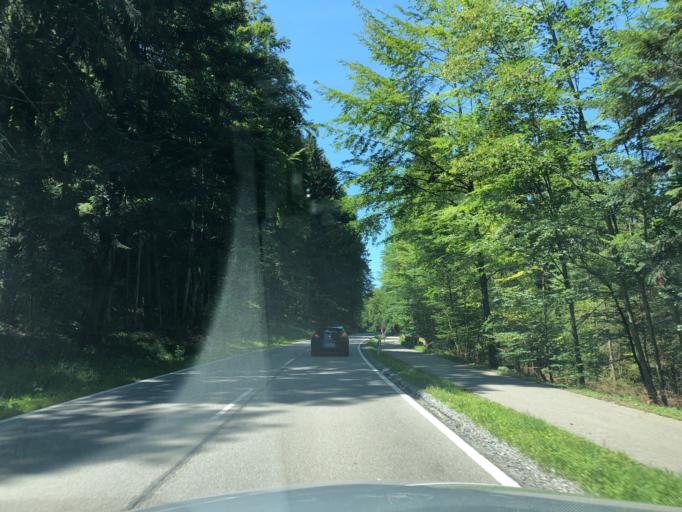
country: DE
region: Bavaria
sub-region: Upper Bavaria
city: Aschau im Chiemgau
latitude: 47.7925
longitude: 12.3067
